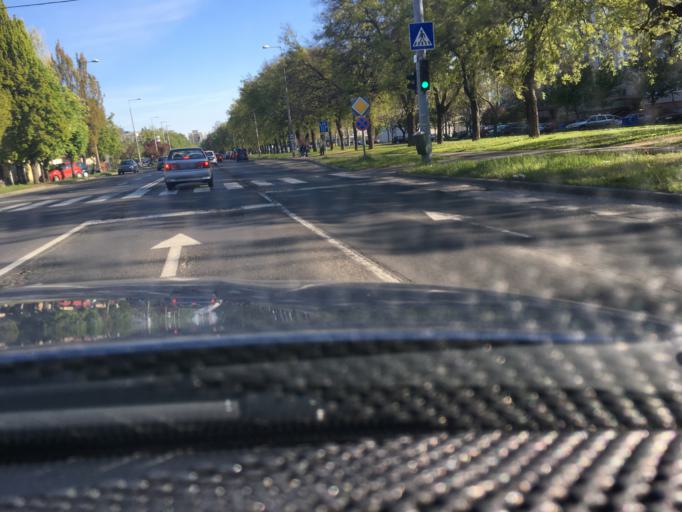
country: HU
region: Hajdu-Bihar
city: Debrecen
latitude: 47.5457
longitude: 21.6097
